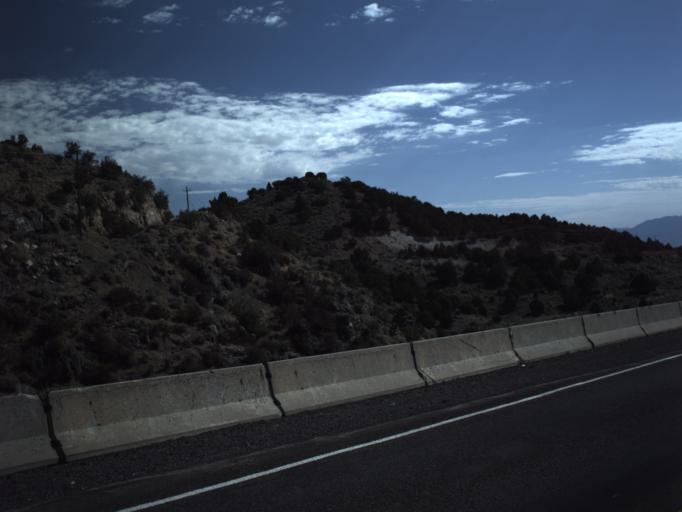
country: US
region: Utah
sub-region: Utah County
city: Genola
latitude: 39.9757
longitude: -112.0719
